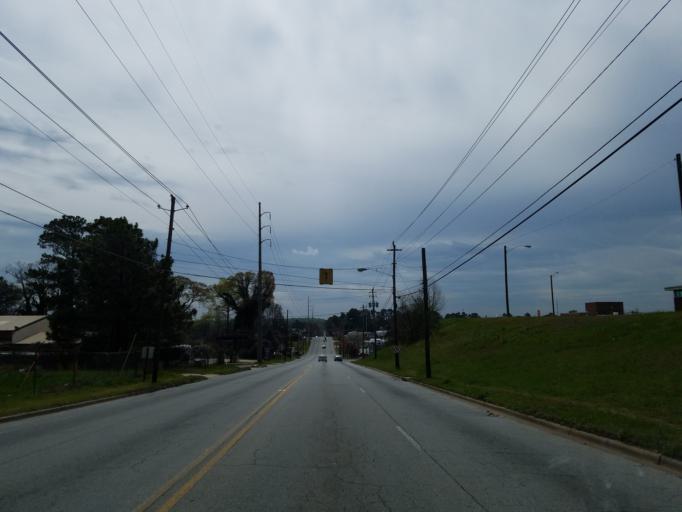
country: US
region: Georgia
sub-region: Fulton County
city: East Point
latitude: 33.6955
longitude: -84.4184
